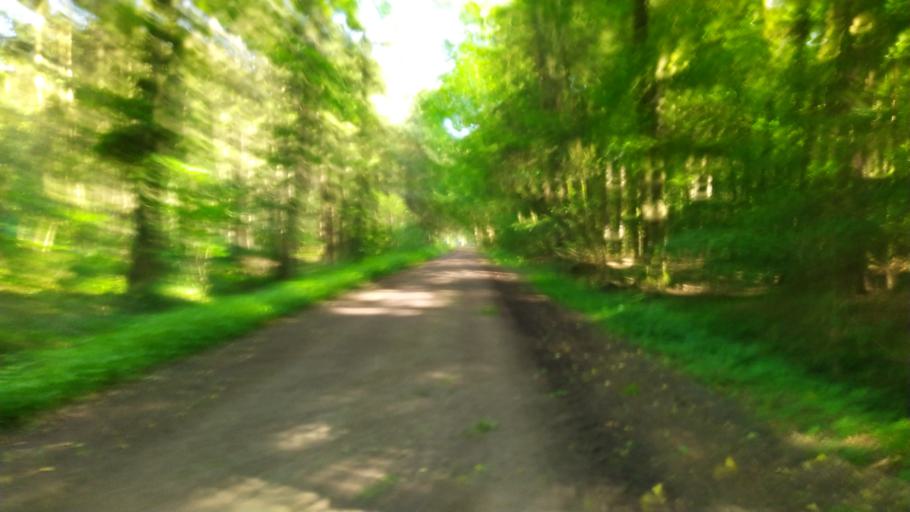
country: DE
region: Lower Saxony
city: Ahlerstedt
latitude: 53.4250
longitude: 9.4749
